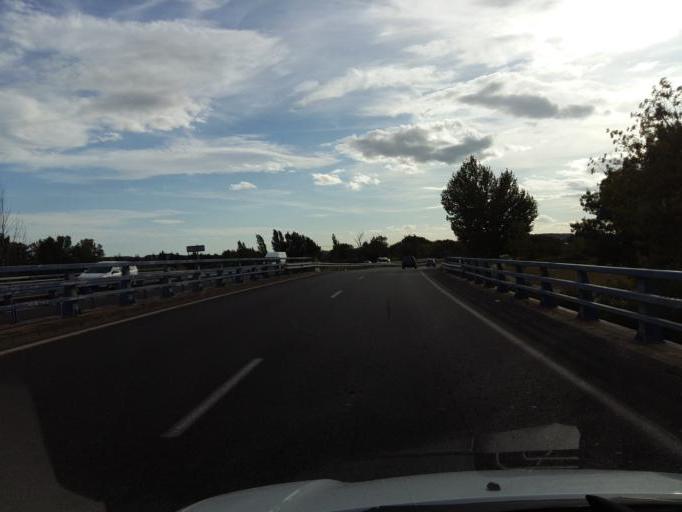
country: FR
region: Provence-Alpes-Cote d'Azur
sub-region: Departement du Vaucluse
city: Althen-des-Paluds
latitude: 43.9973
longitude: 4.9397
